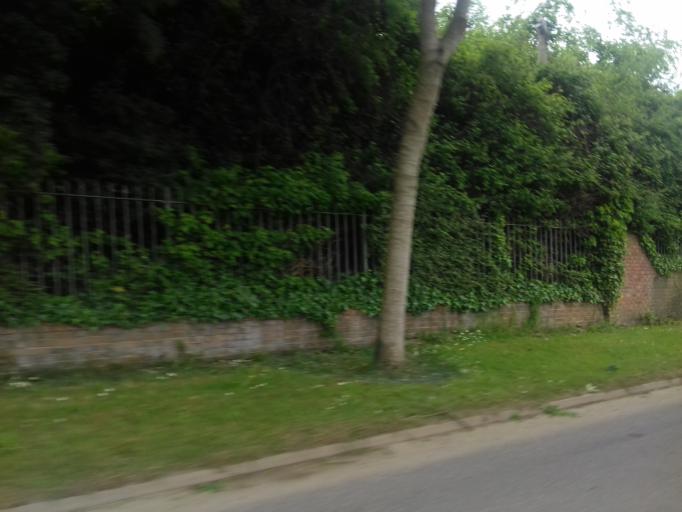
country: IE
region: Leinster
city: Donabate
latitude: 53.4843
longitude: -6.1456
